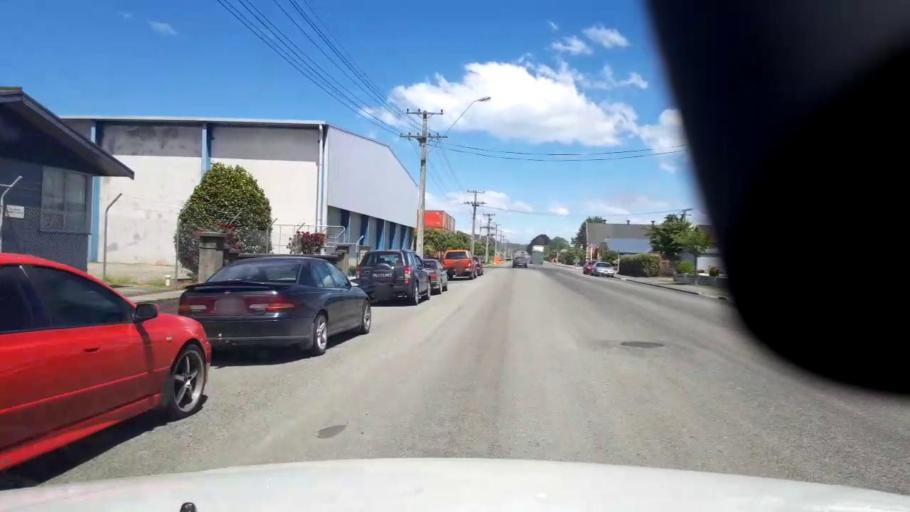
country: NZ
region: Canterbury
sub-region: Timaru District
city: Pleasant Point
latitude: -44.2381
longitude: 171.2793
